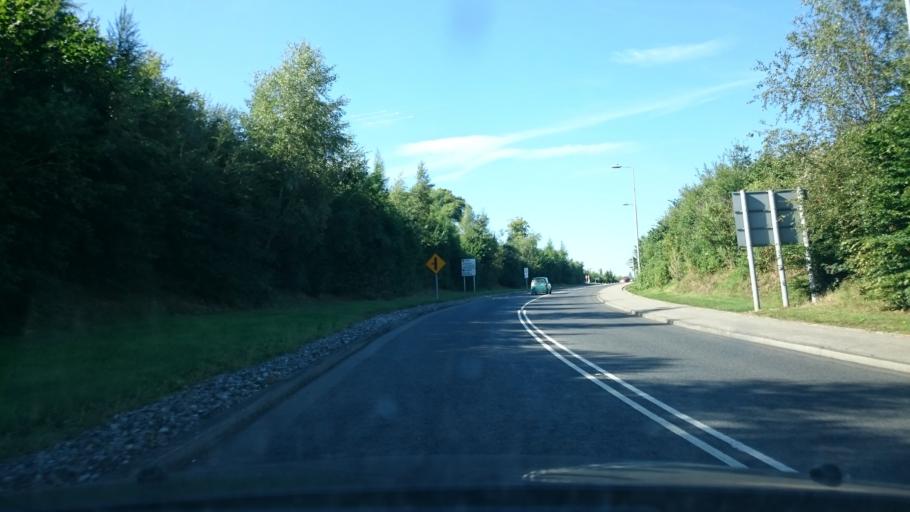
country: IE
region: Leinster
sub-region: Kilkenny
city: Graiguenamanagh
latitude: 52.5382
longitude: -6.9641
